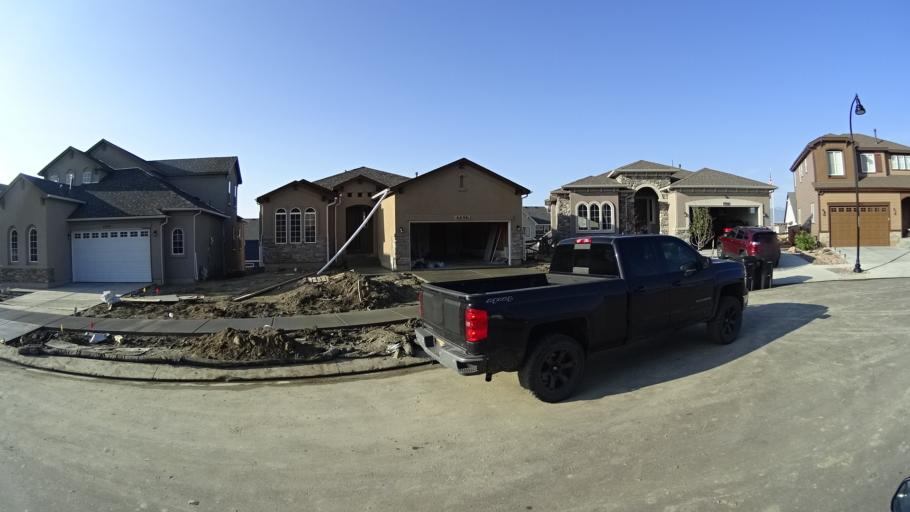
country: US
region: Colorado
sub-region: El Paso County
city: Cimarron Hills
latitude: 38.9293
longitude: -104.6552
